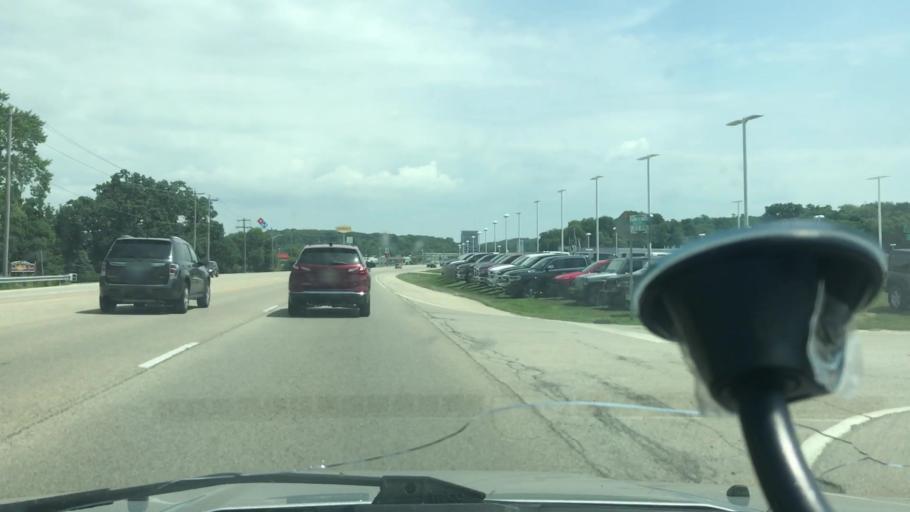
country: US
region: Illinois
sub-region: Tazewell County
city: North Pekin
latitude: 40.6219
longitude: -89.6235
